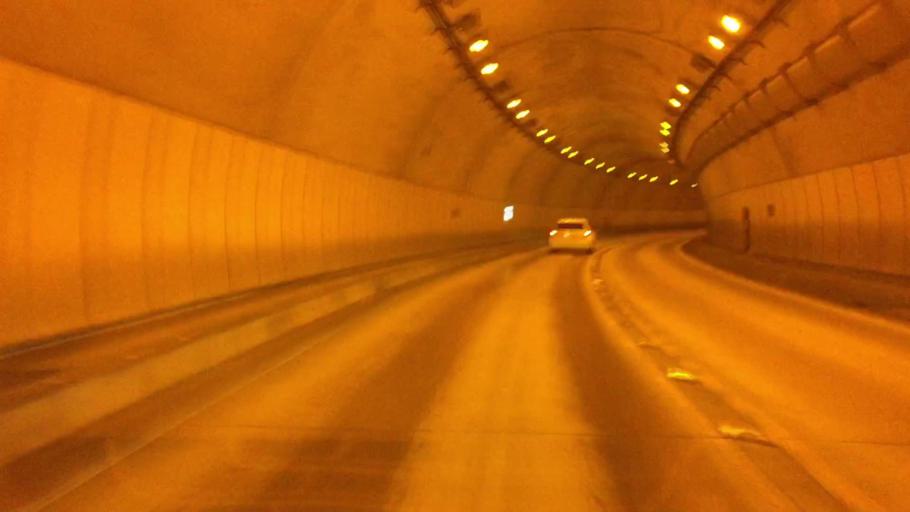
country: JP
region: Tochigi
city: Imaichi
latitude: 36.8212
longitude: 139.7070
